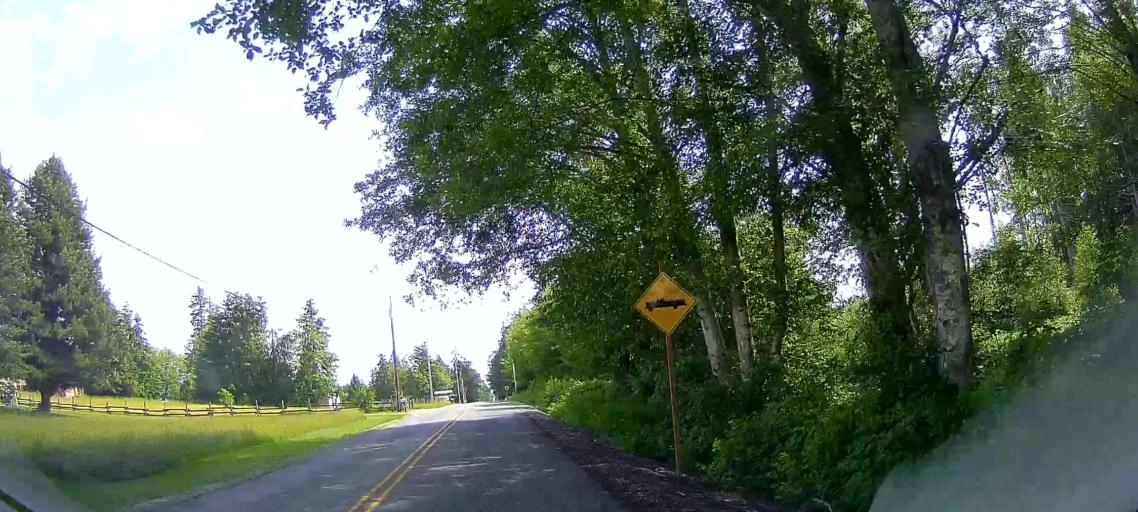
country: US
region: Washington
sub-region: Skagit County
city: Burlington
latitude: 48.5612
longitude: -122.3618
